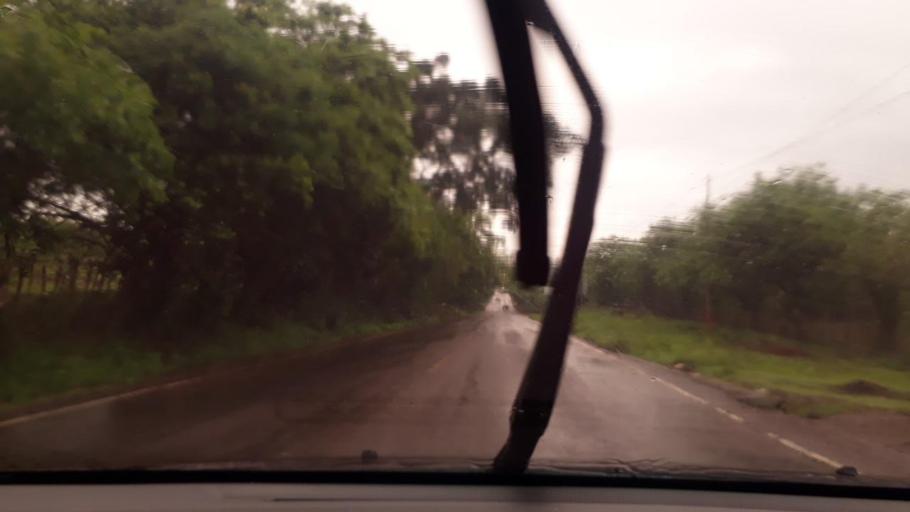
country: GT
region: Jutiapa
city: Comapa
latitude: 14.0493
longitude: -89.9287
